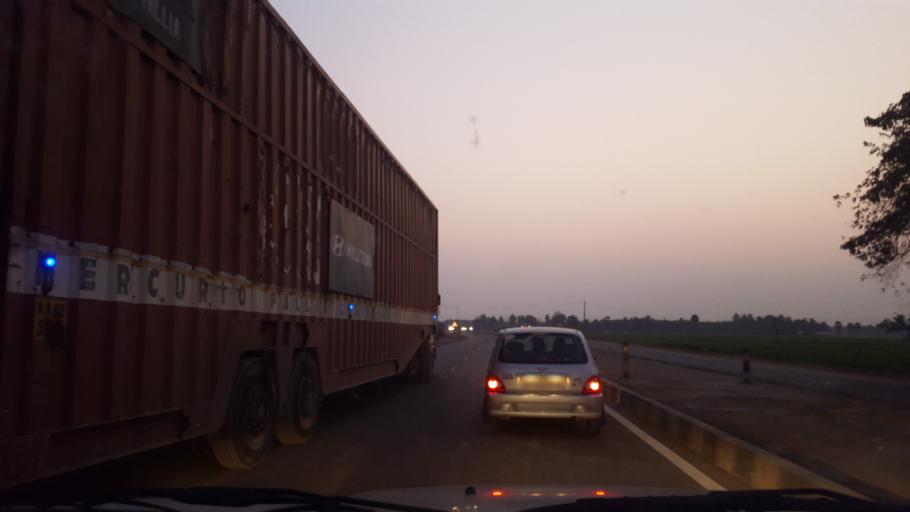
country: IN
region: Andhra Pradesh
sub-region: East Godavari
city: Peddapuram
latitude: 17.1467
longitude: 81.9806
